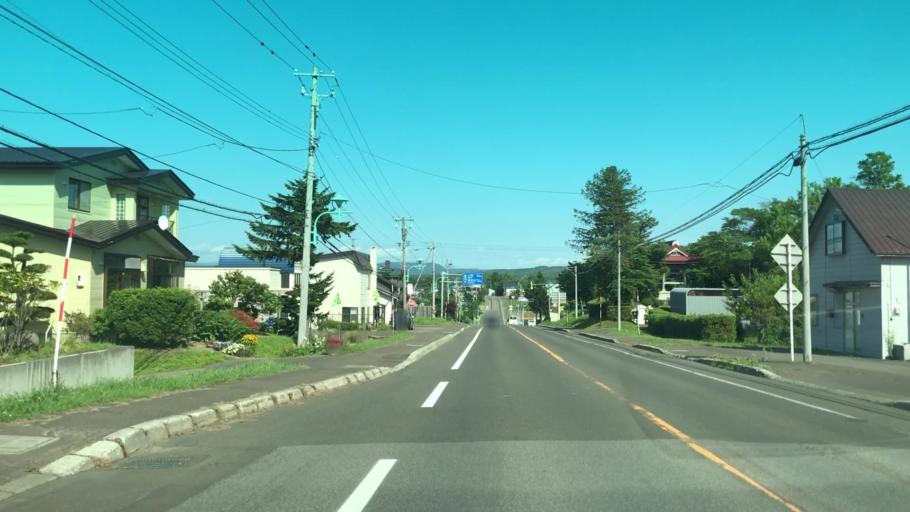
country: JP
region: Hokkaido
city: Iwanai
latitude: 42.9812
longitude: 140.5746
